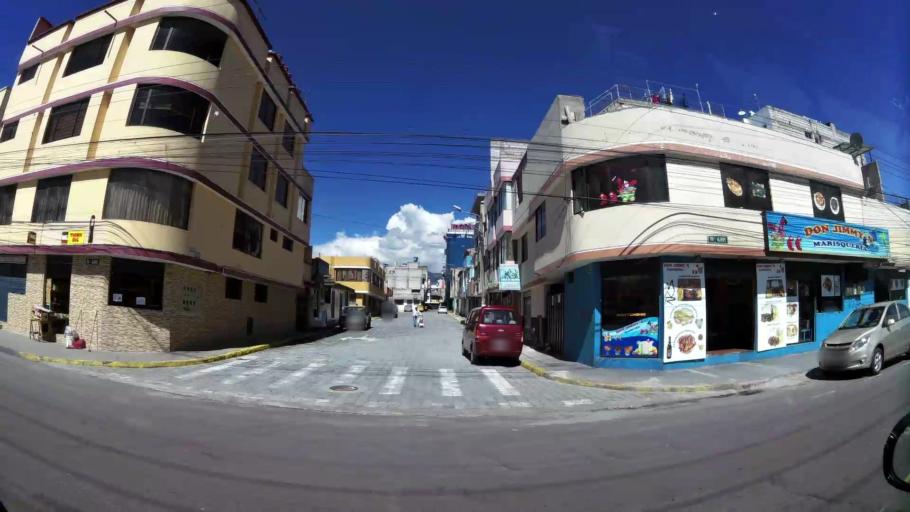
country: EC
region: Pichincha
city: Quito
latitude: -0.2584
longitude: -78.5410
